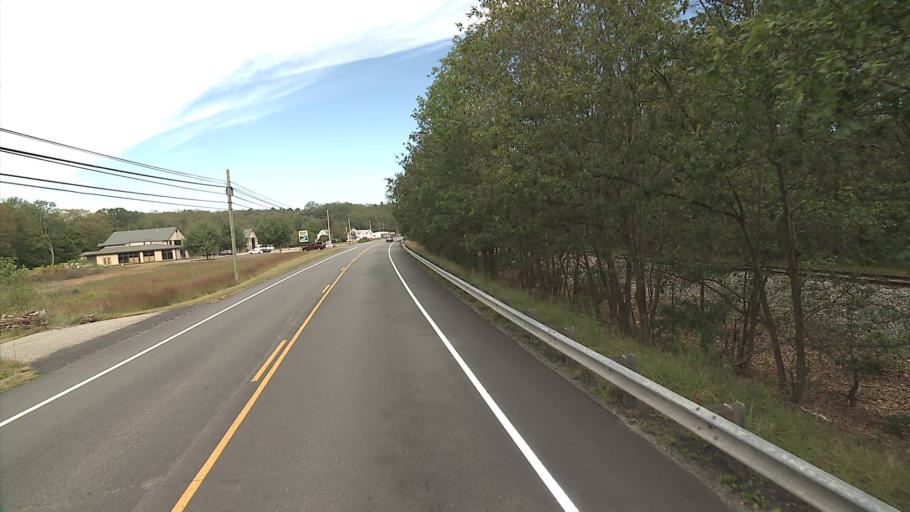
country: US
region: Connecticut
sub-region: Windham County
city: South Windham
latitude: 41.6907
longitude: -72.1789
